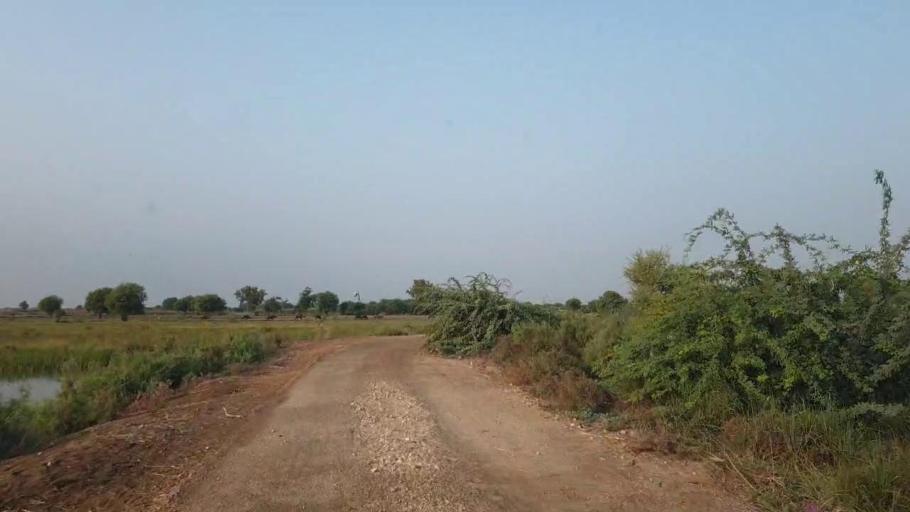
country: PK
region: Sindh
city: Rajo Khanani
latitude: 25.0362
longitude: 68.9633
